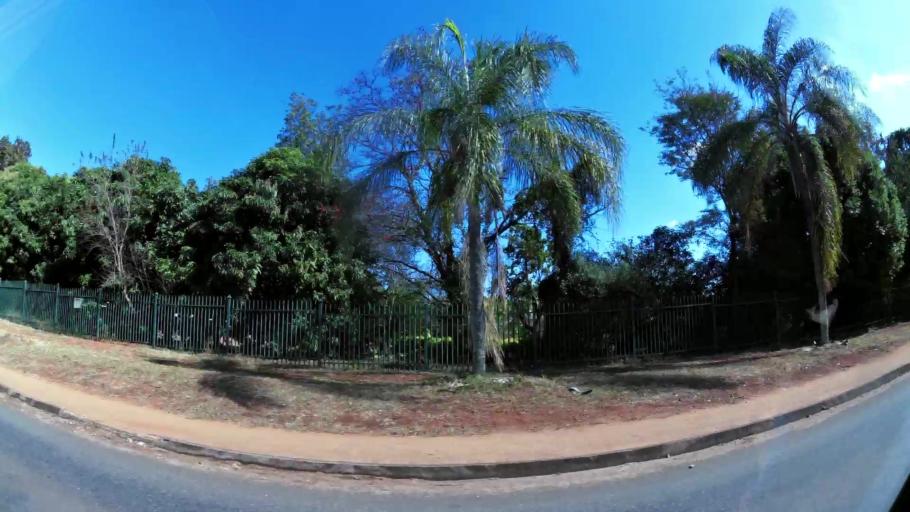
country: ZA
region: Limpopo
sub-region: Mopani District Municipality
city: Tzaneen
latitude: -23.8192
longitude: 30.1584
